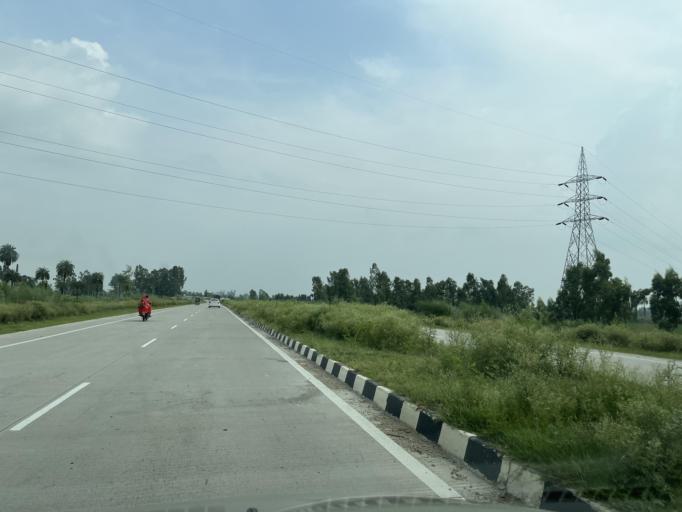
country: IN
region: Uttarakhand
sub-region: Udham Singh Nagar
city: Kashipur
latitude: 29.1674
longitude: 78.9567
